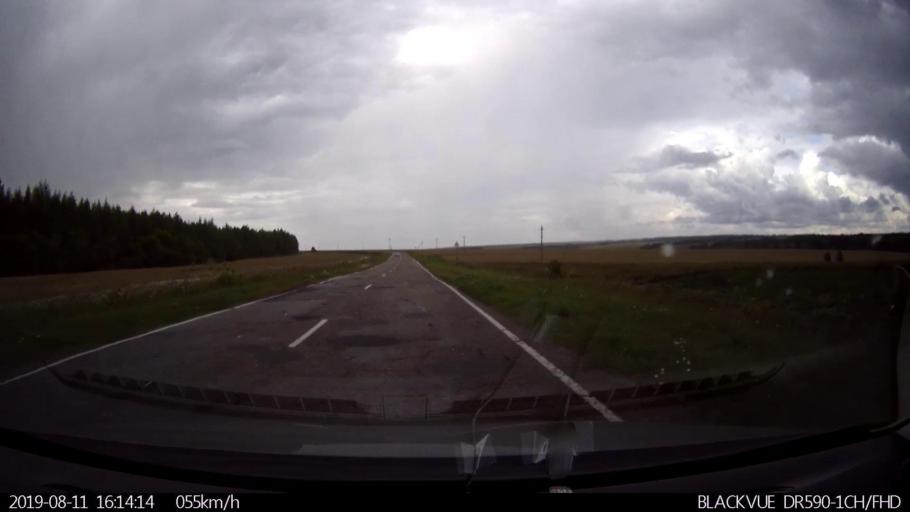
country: RU
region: Ulyanovsk
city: Ignatovka
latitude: 54.0264
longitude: 47.6346
